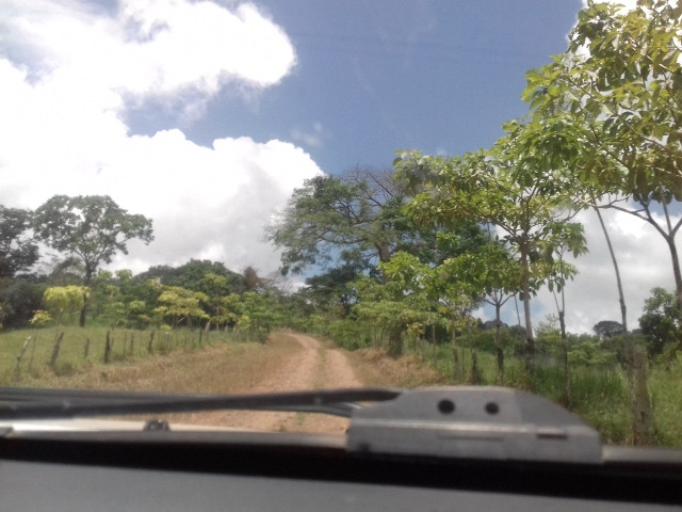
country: NI
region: Matagalpa
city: Matiguas
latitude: 13.0087
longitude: -85.3935
